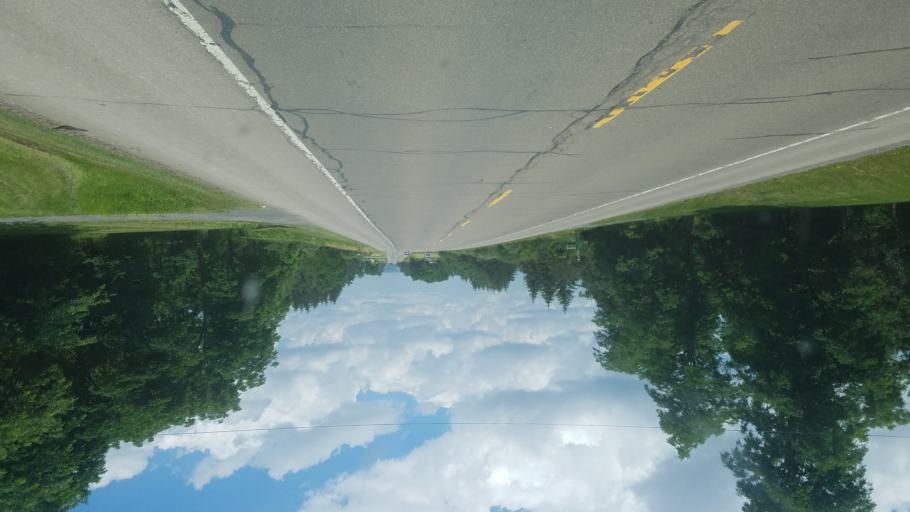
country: US
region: New York
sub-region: Yates County
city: Keuka Park
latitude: 42.5805
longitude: -77.0364
